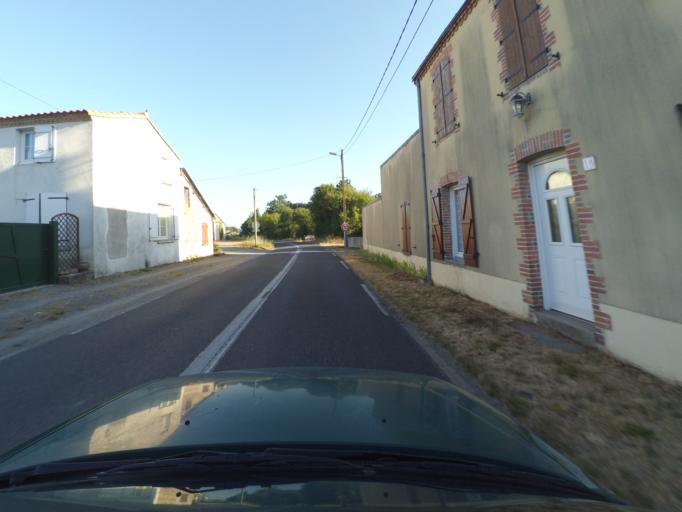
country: FR
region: Pays de la Loire
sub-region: Departement de la Loire-Atlantique
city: Montbert
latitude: 47.0375
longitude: -1.4696
